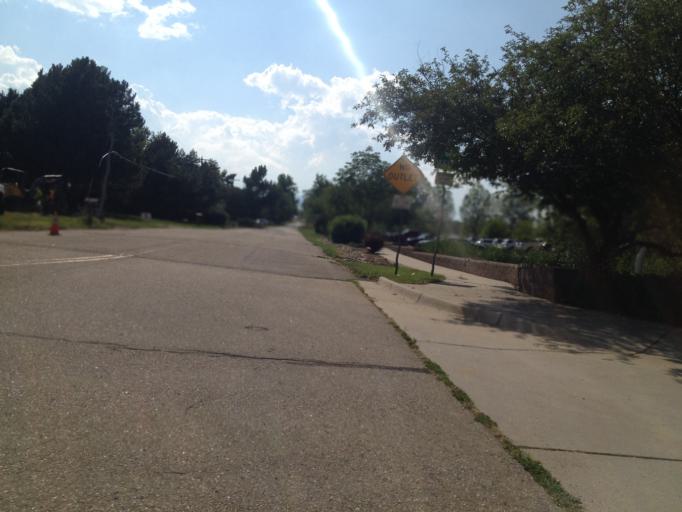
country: US
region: Colorado
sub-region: Boulder County
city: Superior
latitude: 39.9624
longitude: -105.1703
